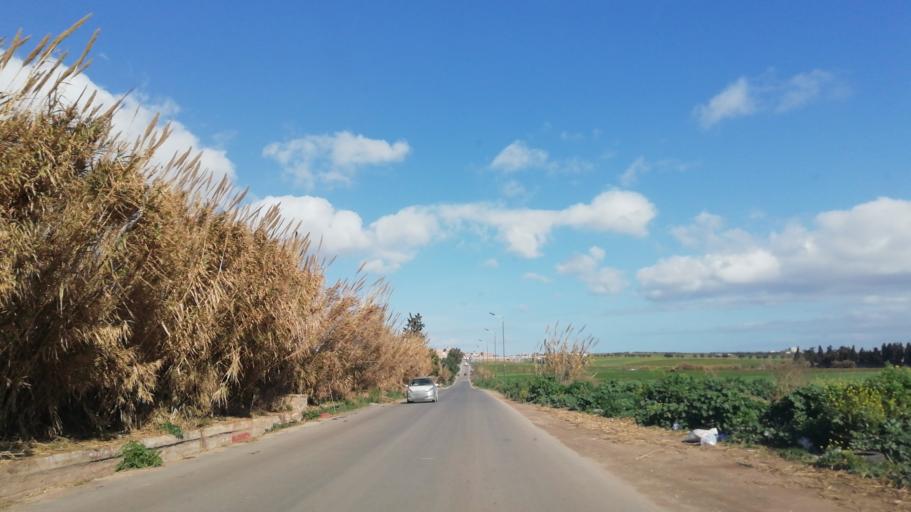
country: DZ
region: Oran
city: Es Senia
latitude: 35.6251
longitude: -0.6615
